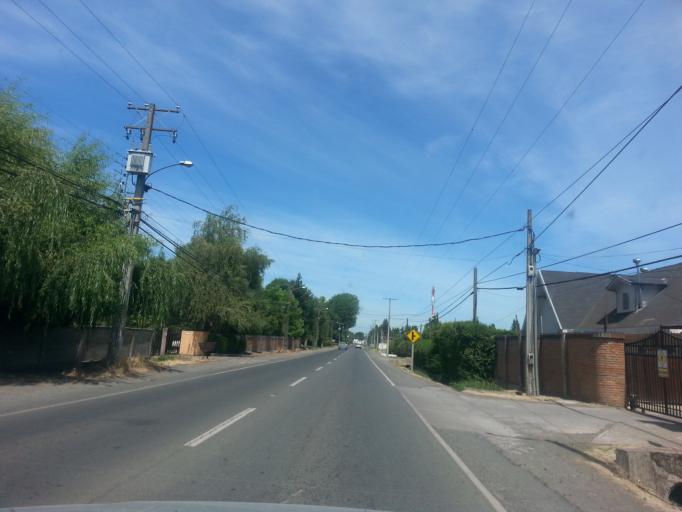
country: CL
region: Biobio
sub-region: Provincia de Nuble
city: Chillan
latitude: -36.5894
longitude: -72.0619
